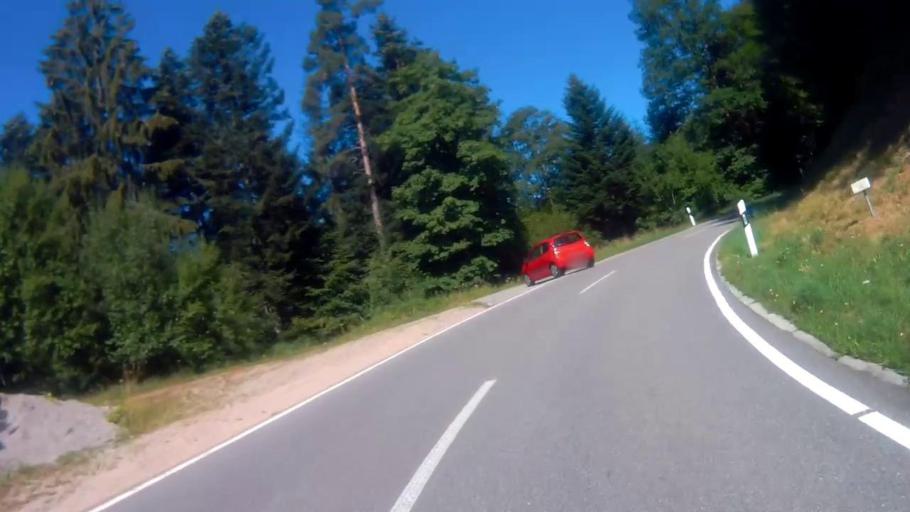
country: DE
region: Baden-Wuerttemberg
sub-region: Freiburg Region
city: Badenweiler
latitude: 47.7830
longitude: 7.7300
